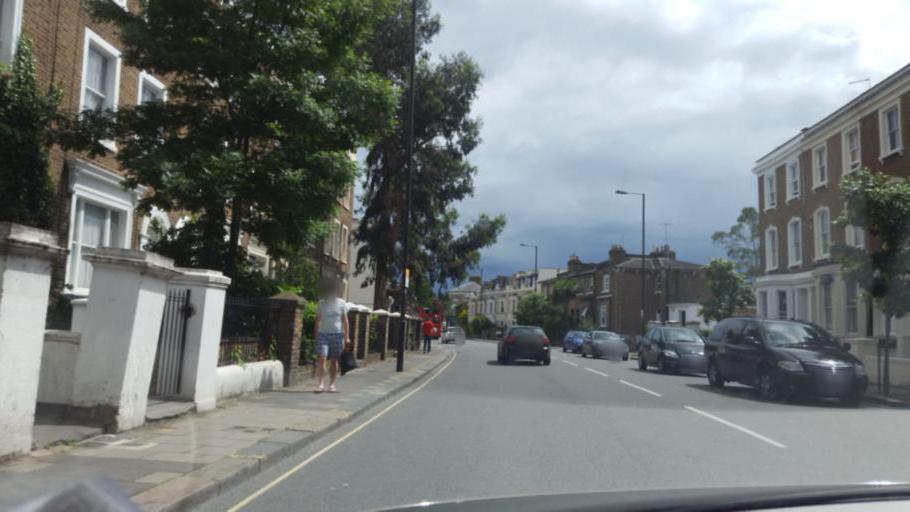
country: GB
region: England
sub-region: Greater London
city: Hammersmith
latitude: 51.5056
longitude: -0.2446
